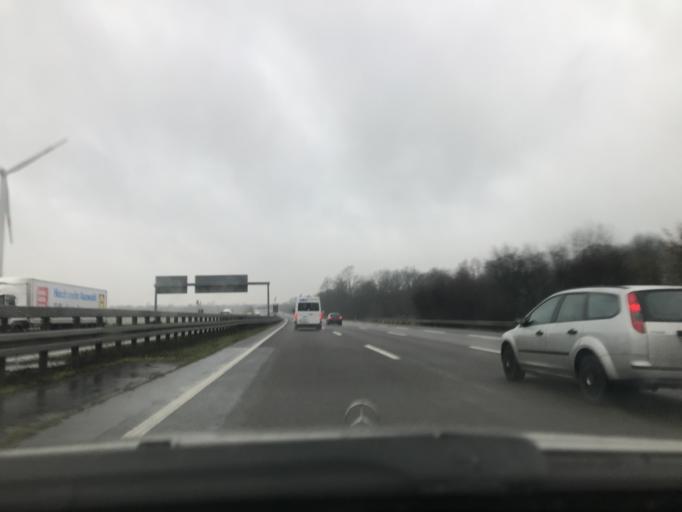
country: DE
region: North Rhine-Westphalia
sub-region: Regierungsbezirk Dusseldorf
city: Moers
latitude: 51.4944
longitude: 6.6279
